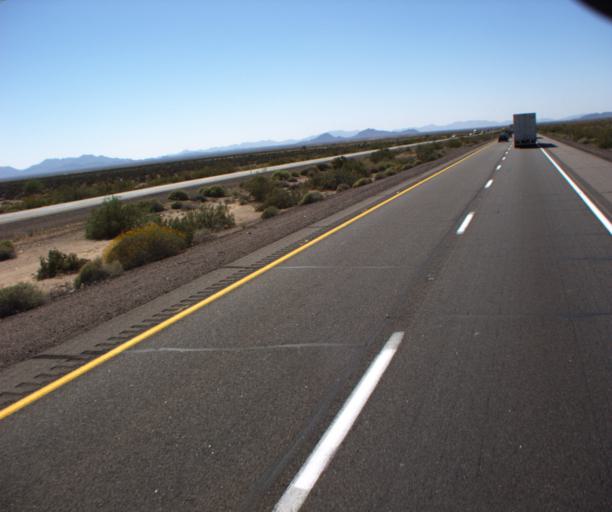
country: US
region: Arizona
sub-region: Yuma County
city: Wellton
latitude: 32.7167
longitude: -113.8016
